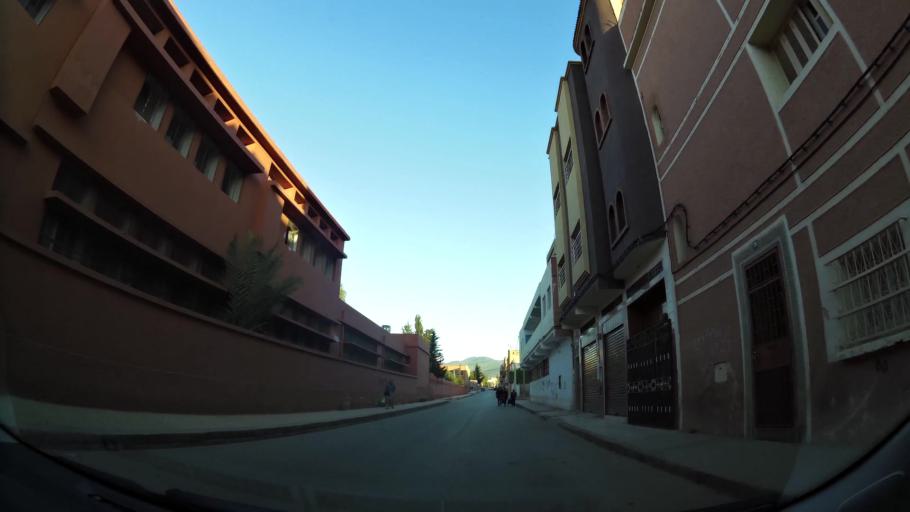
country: MA
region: Oriental
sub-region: Berkane-Taourirt
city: Berkane
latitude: 34.9270
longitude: -2.3293
